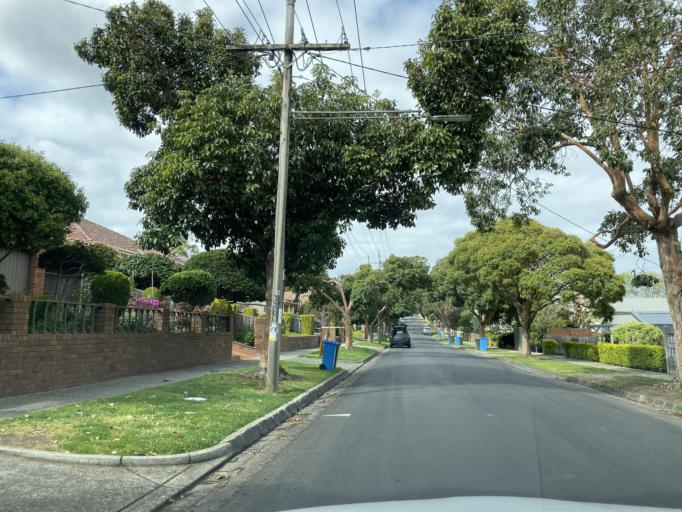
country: AU
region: Victoria
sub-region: Boroondara
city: Ashburton
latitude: -37.8505
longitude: 145.0870
